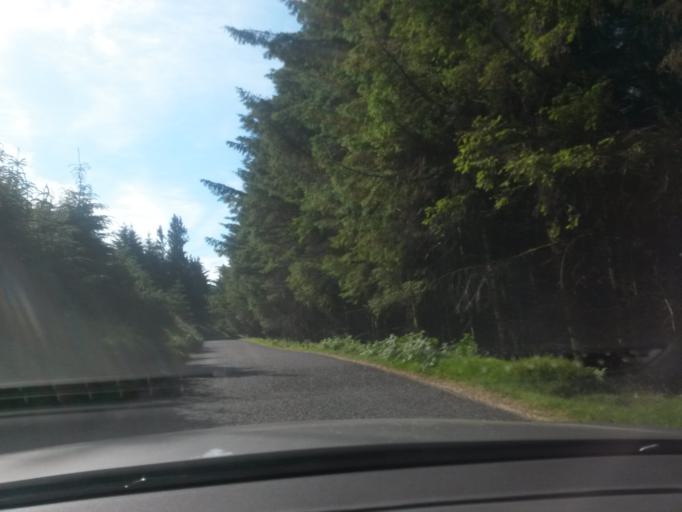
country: IE
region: Leinster
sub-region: Wicklow
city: Enniskerry
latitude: 53.1169
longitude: -6.2665
